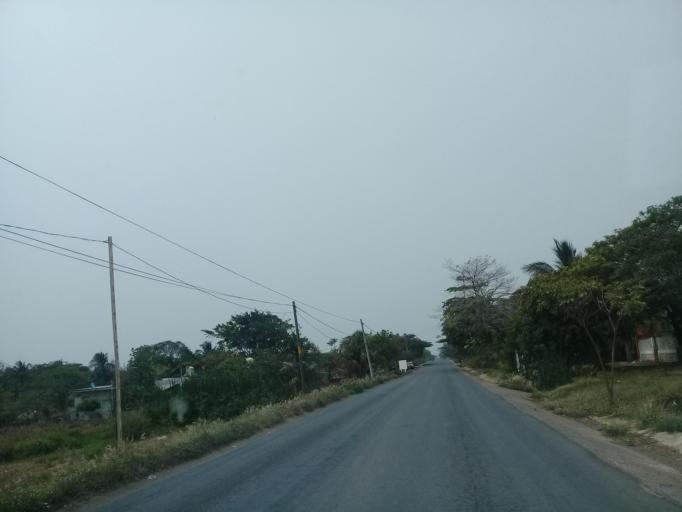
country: MX
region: Veracruz
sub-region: Medellin
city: La Laguna y Monte del Castillo
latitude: 18.9810
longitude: -96.1182
